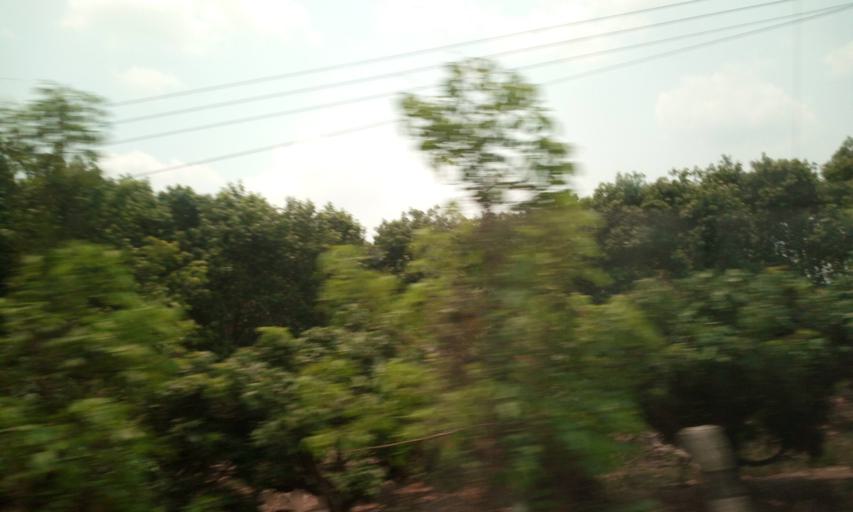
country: TH
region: Phayao
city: Phu Sang
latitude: 19.6084
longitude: 100.2964
